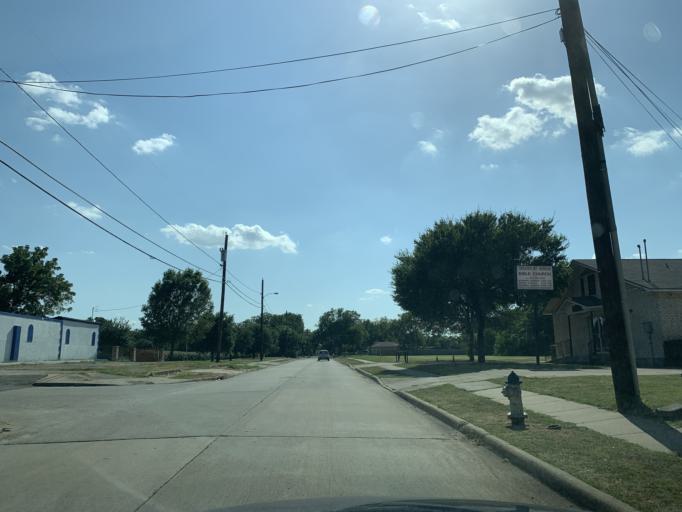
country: US
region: Texas
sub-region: Dallas County
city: Hutchins
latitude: 32.6868
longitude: -96.7826
